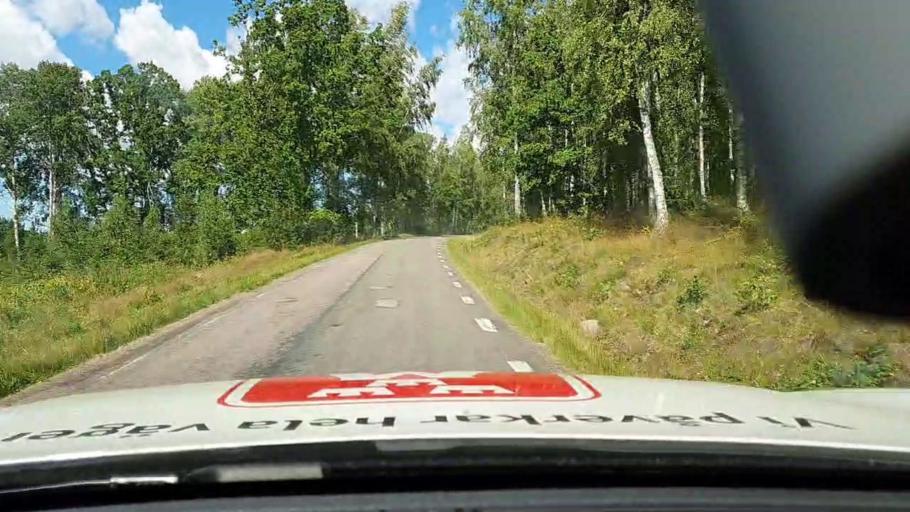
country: SE
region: Vaestra Goetaland
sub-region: Karlsborgs Kommun
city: Molltorp
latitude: 58.5973
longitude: 14.2639
